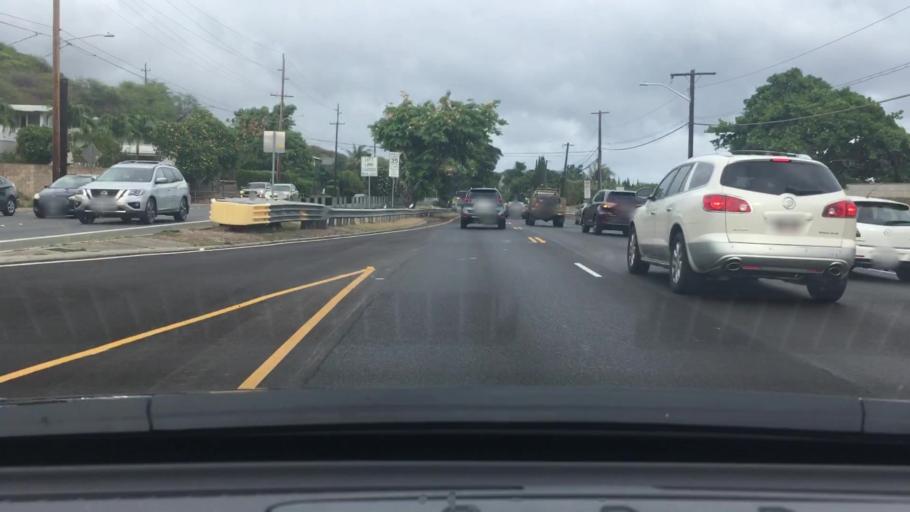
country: US
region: Hawaii
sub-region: Honolulu County
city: Honolulu
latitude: 21.2778
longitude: -157.7794
